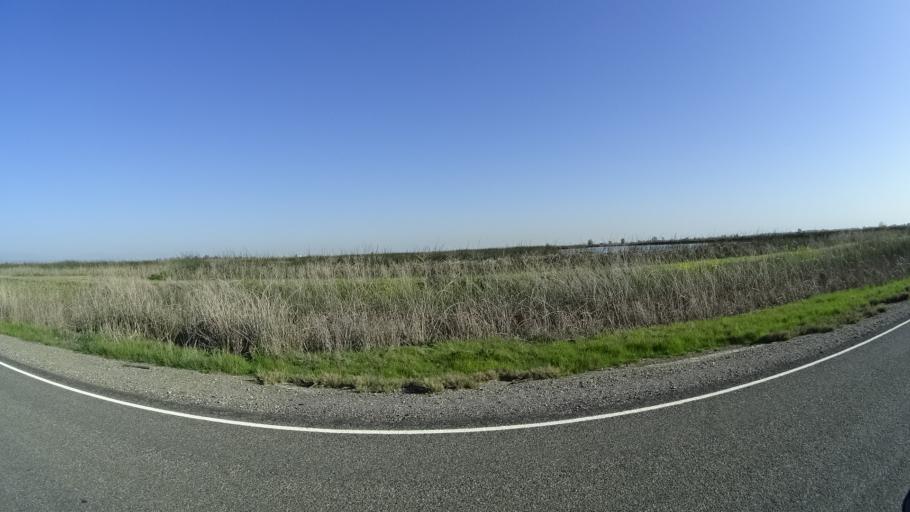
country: US
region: California
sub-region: Glenn County
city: Willows
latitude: 39.4073
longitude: -122.1660
